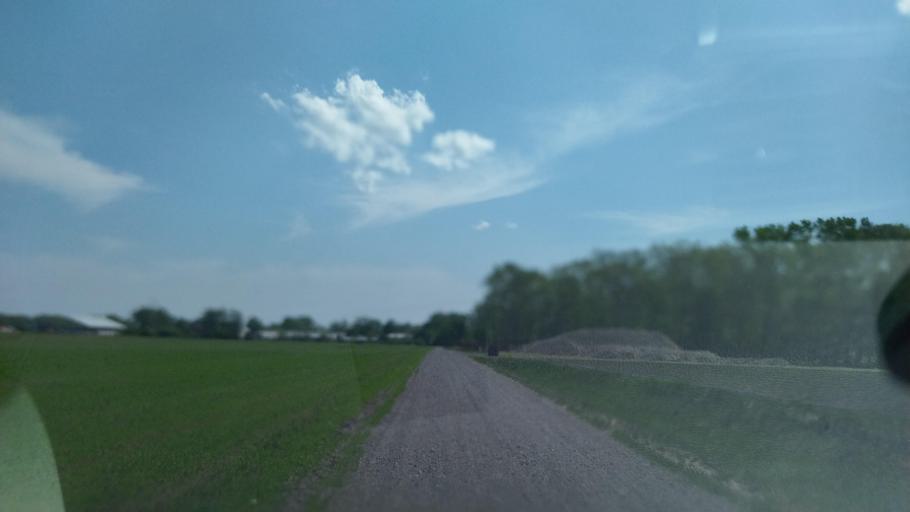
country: JP
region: Hokkaido
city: Otofuke
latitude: 43.1354
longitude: 143.2189
